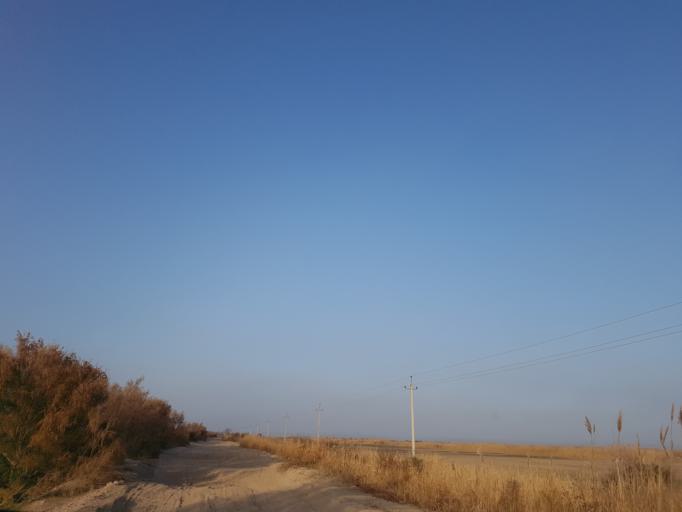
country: TM
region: Dasoguz
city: Koeneuergench
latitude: 41.8513
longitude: 58.2899
